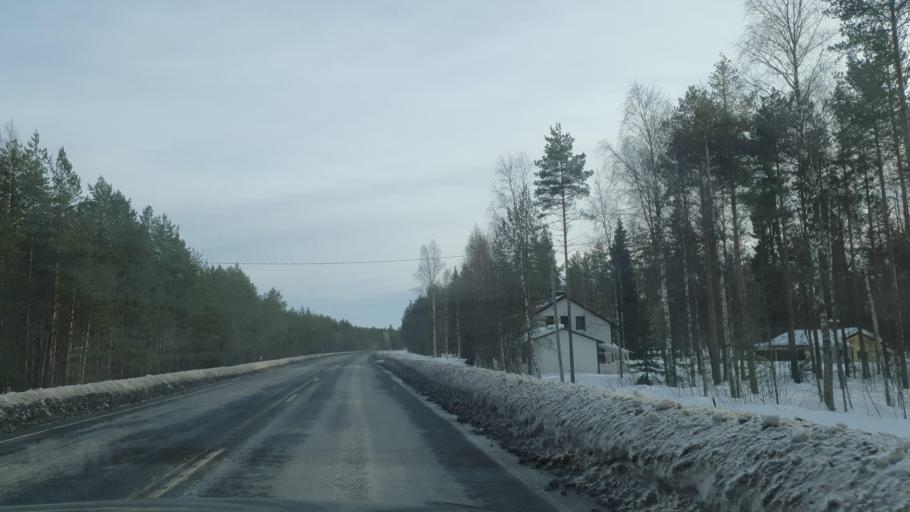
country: FI
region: Northern Ostrobothnia
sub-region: Oulunkaari
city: Utajaervi
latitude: 64.7344
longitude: 26.4731
